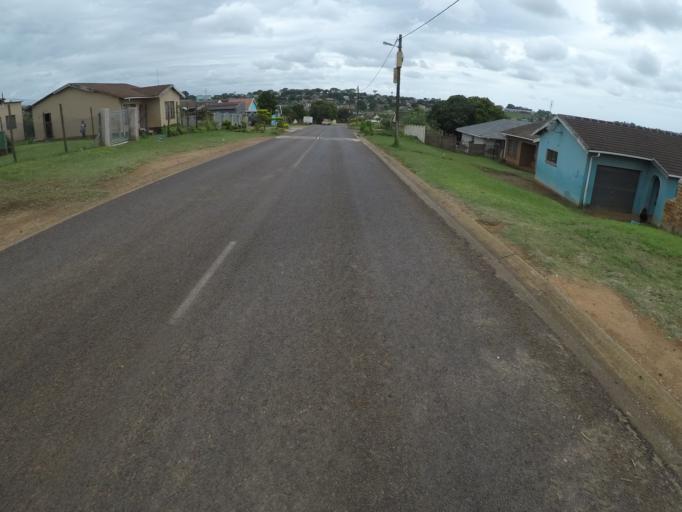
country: ZA
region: KwaZulu-Natal
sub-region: uThungulu District Municipality
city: Empangeni
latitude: -28.7785
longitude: 31.8540
